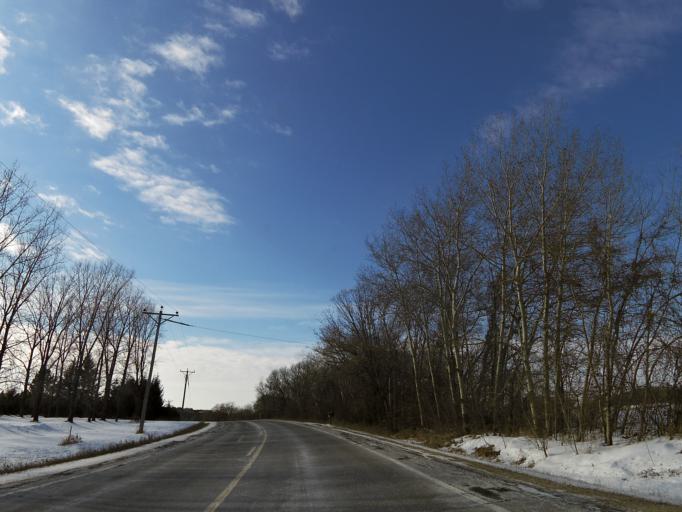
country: US
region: Wisconsin
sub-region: Saint Croix County
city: Roberts
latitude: 44.9926
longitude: -92.6117
